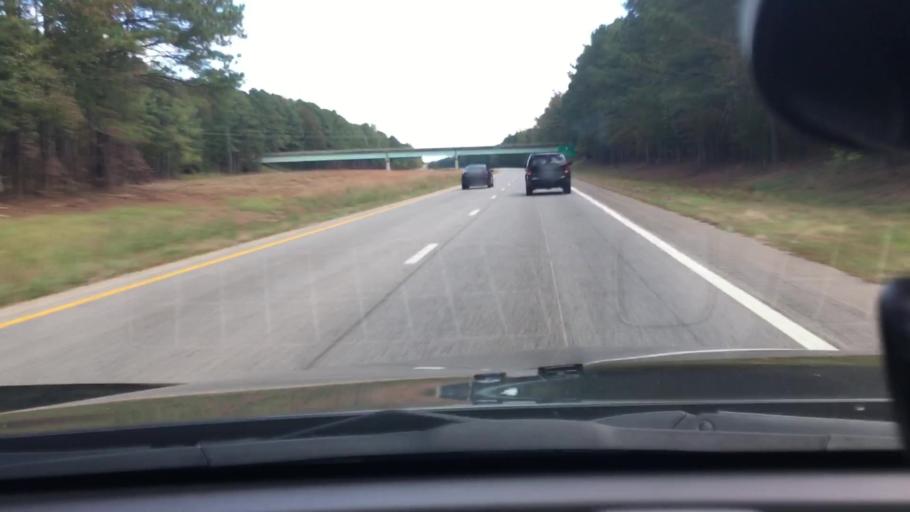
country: US
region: North Carolina
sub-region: Nash County
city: Spring Hope
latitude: 35.7900
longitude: -78.1410
